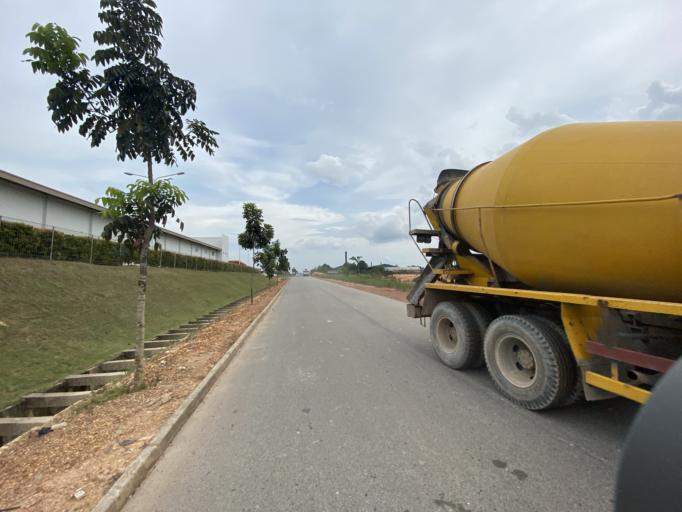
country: SG
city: Singapore
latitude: 1.0225
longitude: 103.9465
